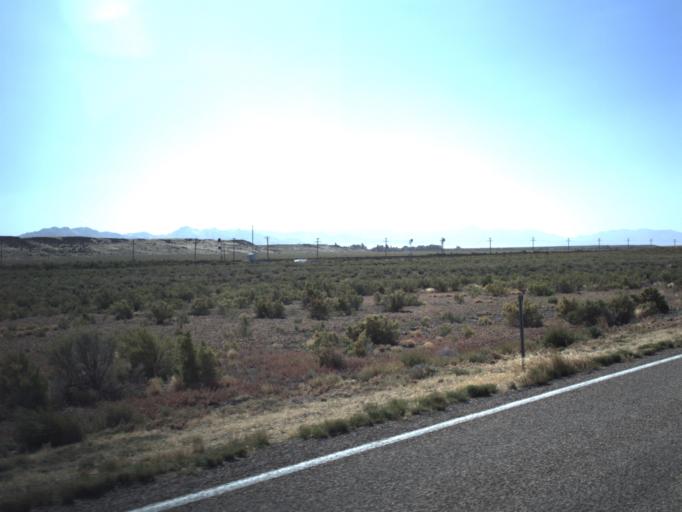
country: US
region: Utah
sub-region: Beaver County
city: Milford
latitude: 38.7287
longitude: -112.9667
